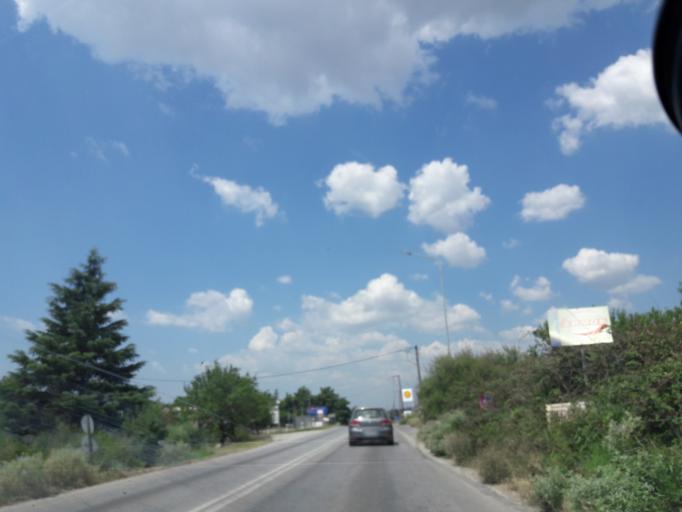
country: GR
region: Central Macedonia
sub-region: Nomos Thessalonikis
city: Souroti
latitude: 40.5040
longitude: 23.0925
